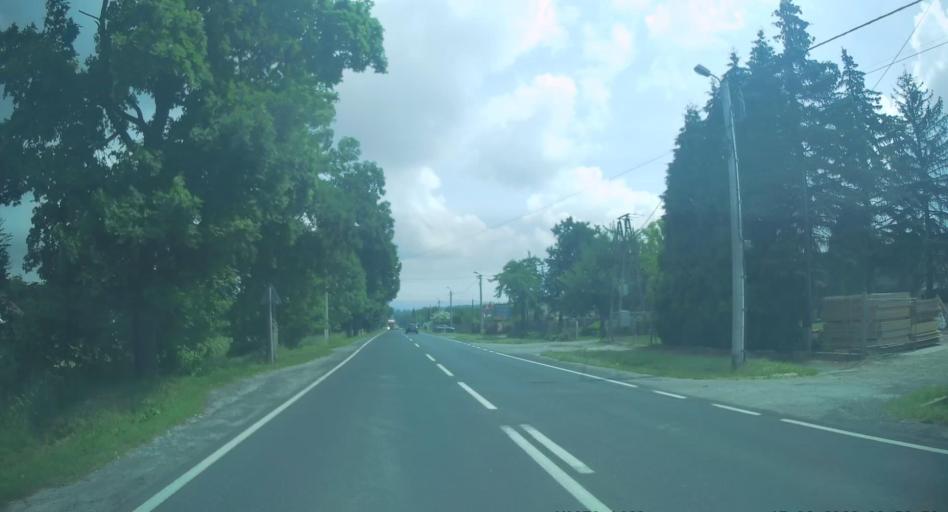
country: PL
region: Lesser Poland Voivodeship
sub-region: Powiat wadowicki
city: Chocznia
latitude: 49.8700
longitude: 19.4436
